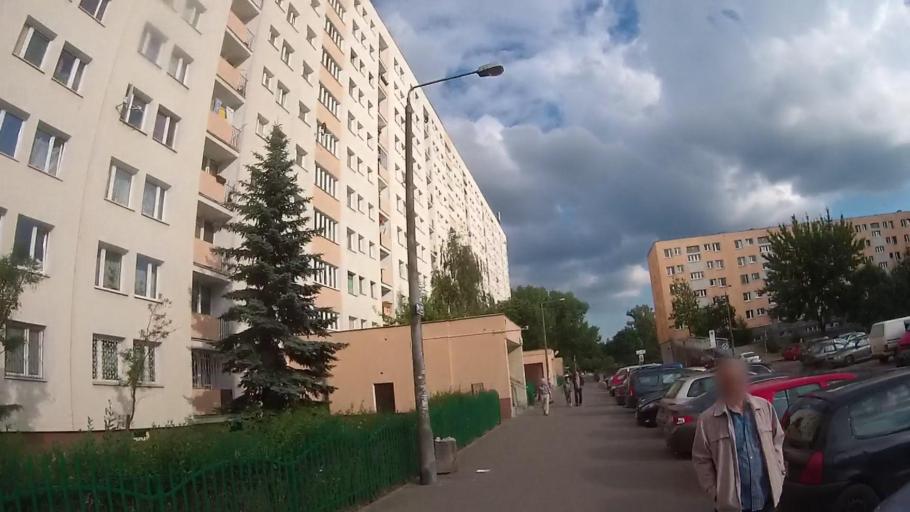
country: PL
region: Masovian Voivodeship
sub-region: Warszawa
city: Praga Polnoc
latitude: 52.2549
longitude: 21.0520
